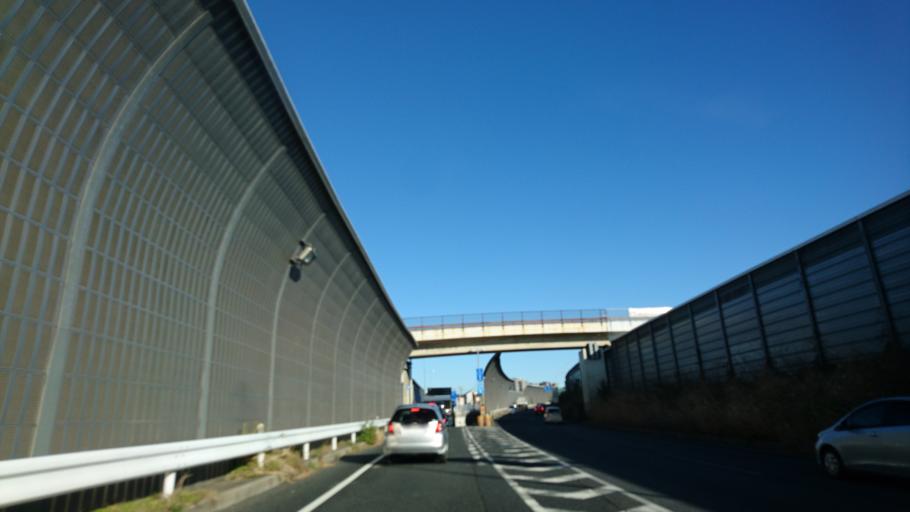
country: JP
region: Chiba
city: Chiba
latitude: 35.5697
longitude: 140.1377
